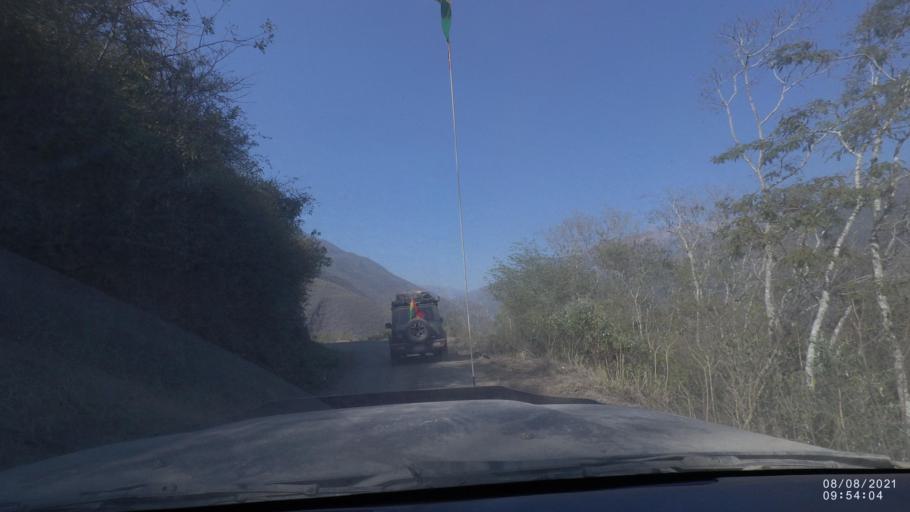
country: BO
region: La Paz
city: Quime
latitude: -16.6316
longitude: -66.7344
